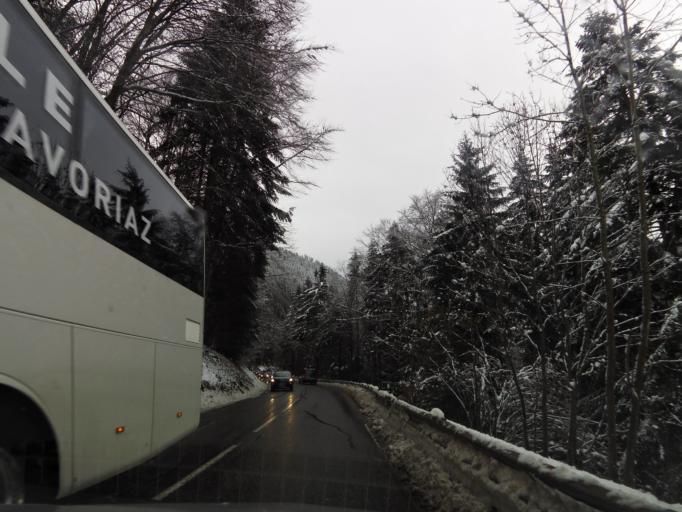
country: FR
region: Rhone-Alpes
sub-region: Departement de la Haute-Savoie
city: Taninges
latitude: 46.1284
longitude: 6.6231
